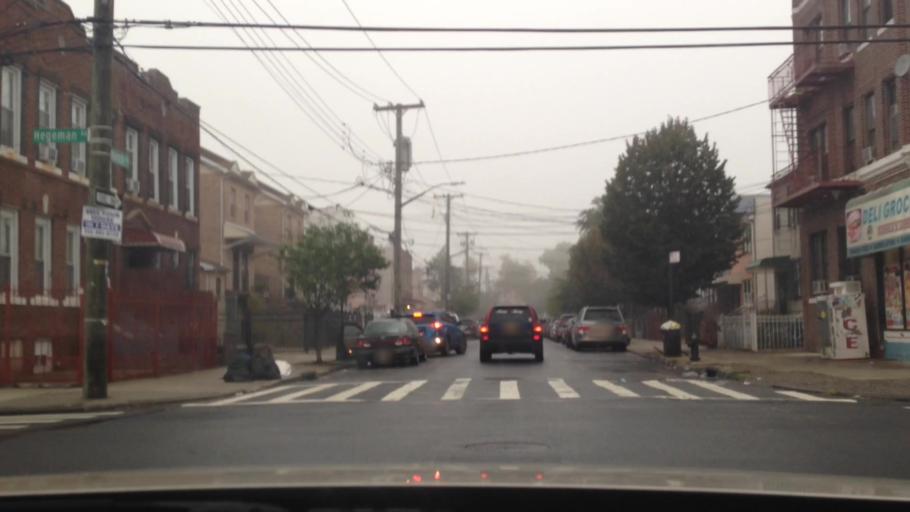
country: US
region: New York
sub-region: Kings County
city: East New York
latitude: 40.6627
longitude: -73.8851
